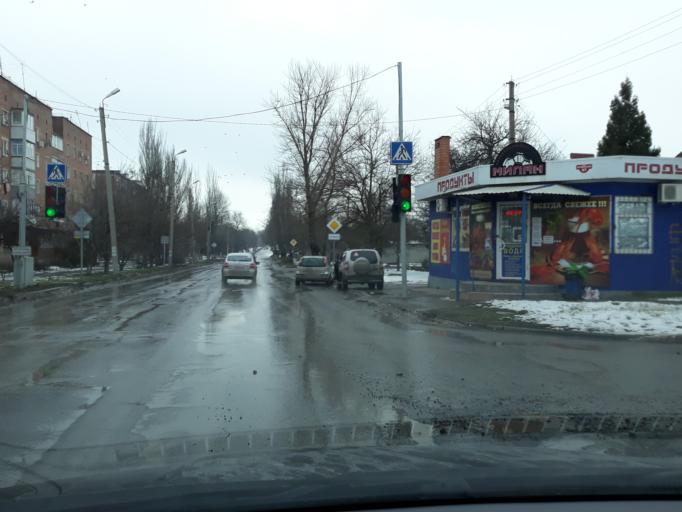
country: RU
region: Rostov
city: Taganrog
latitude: 47.2254
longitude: 38.9019
